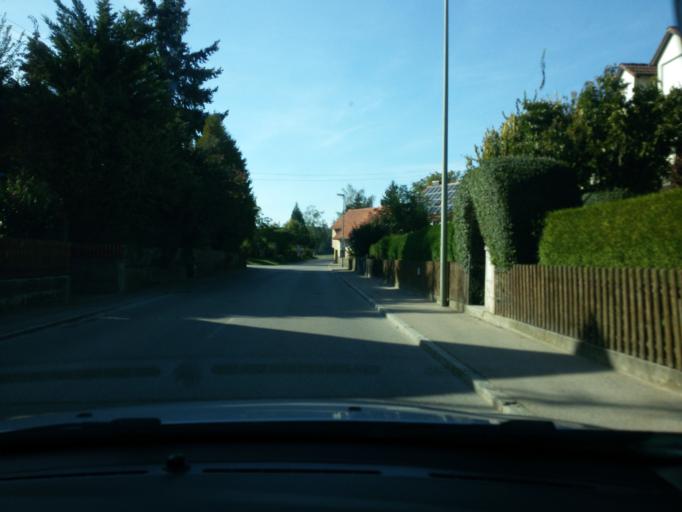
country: DE
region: Bavaria
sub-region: Swabia
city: Gessertshausen
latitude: 48.3457
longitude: 10.7296
